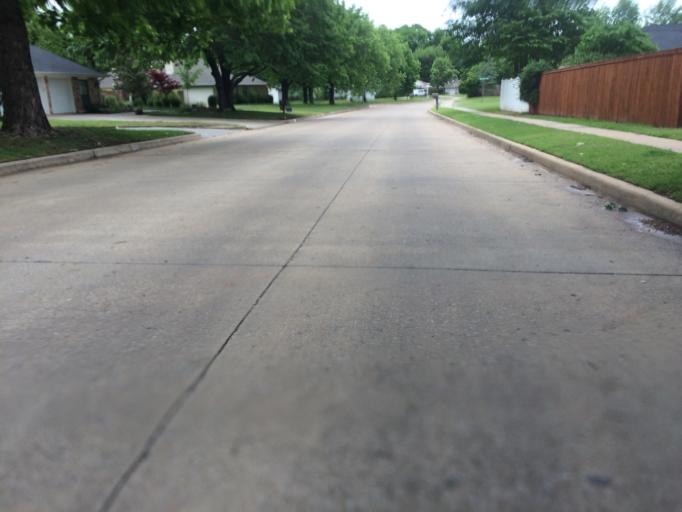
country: US
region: Oklahoma
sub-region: Cleveland County
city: Norman
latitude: 35.1881
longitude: -97.4565
